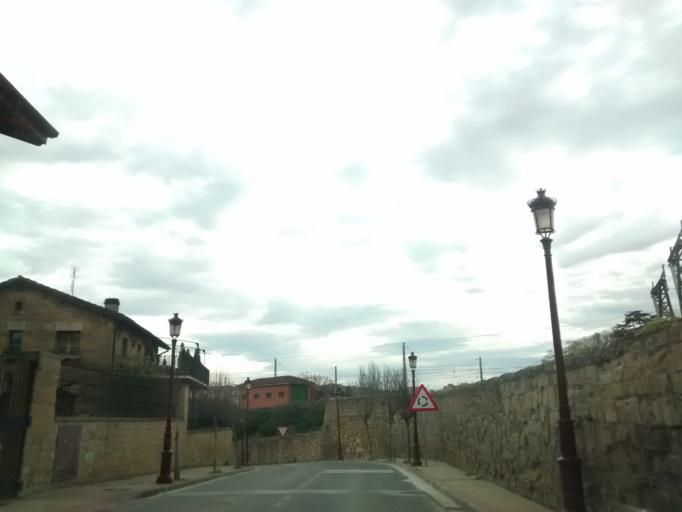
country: ES
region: La Rioja
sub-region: Provincia de La Rioja
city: Haro
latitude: 42.5837
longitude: -2.8477
